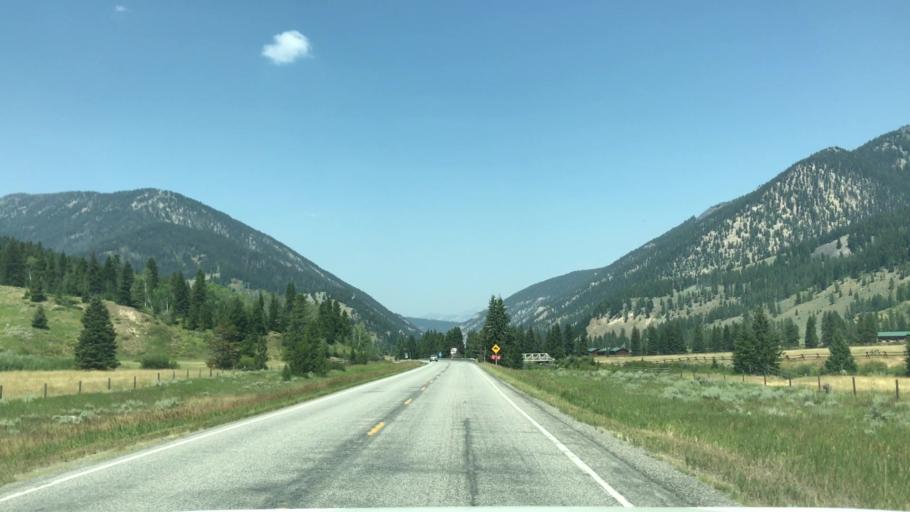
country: US
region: Montana
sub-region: Gallatin County
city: Big Sky
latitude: 45.0983
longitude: -111.2171
